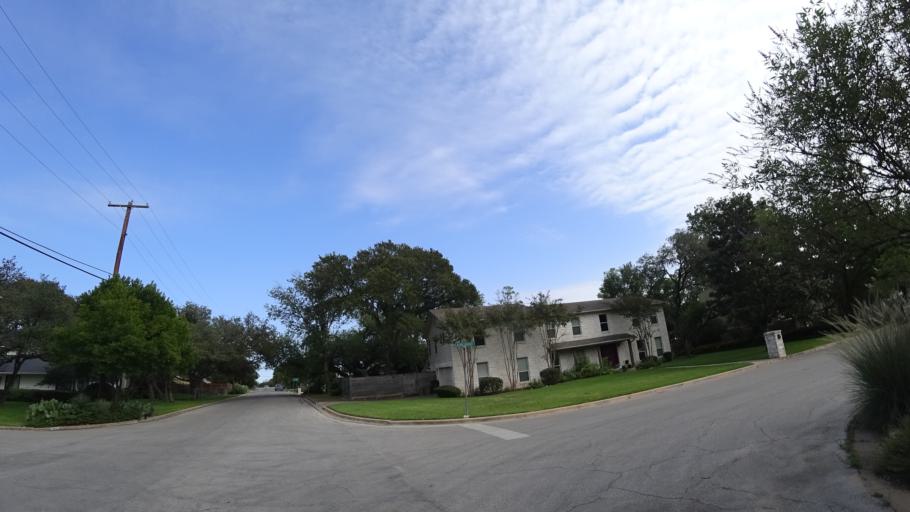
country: US
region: Texas
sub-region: Travis County
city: Rollingwood
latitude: 30.2798
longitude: -97.8038
